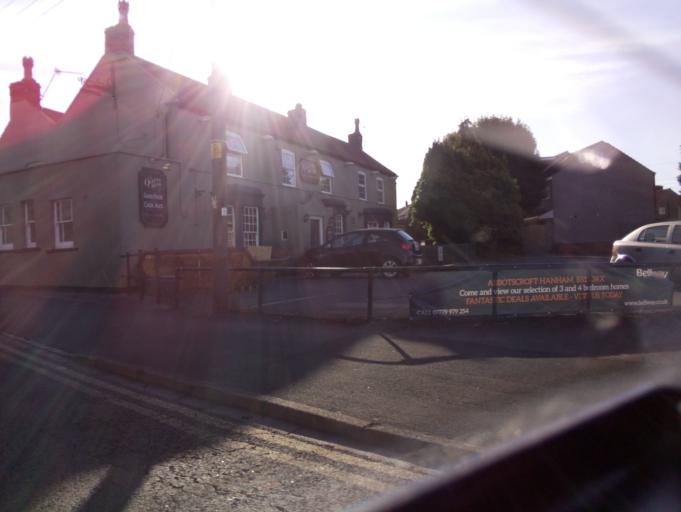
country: GB
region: England
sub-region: South Gloucestershire
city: Kingswood
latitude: 51.4512
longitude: -2.5143
